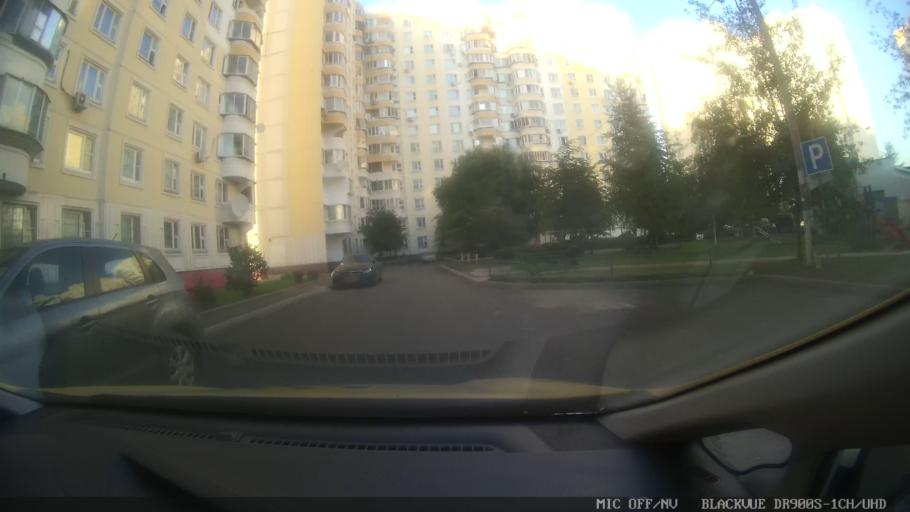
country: RU
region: Moscow
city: Nekrasovka
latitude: 55.6968
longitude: 37.9078
